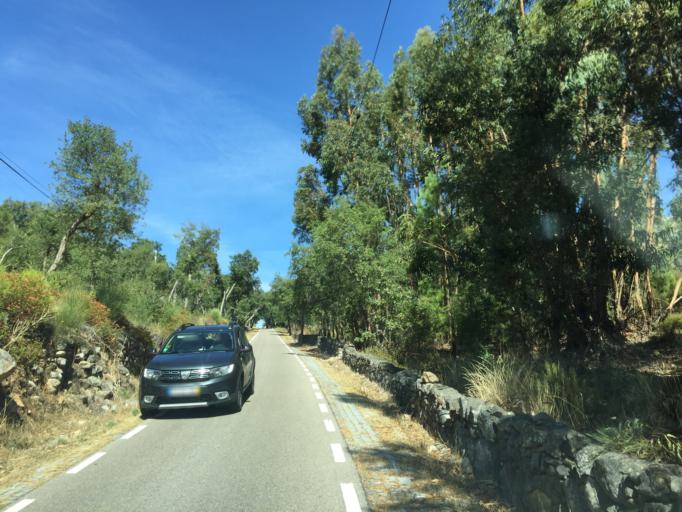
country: PT
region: Portalegre
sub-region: Marvao
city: Marvao
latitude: 39.3983
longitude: -7.3896
